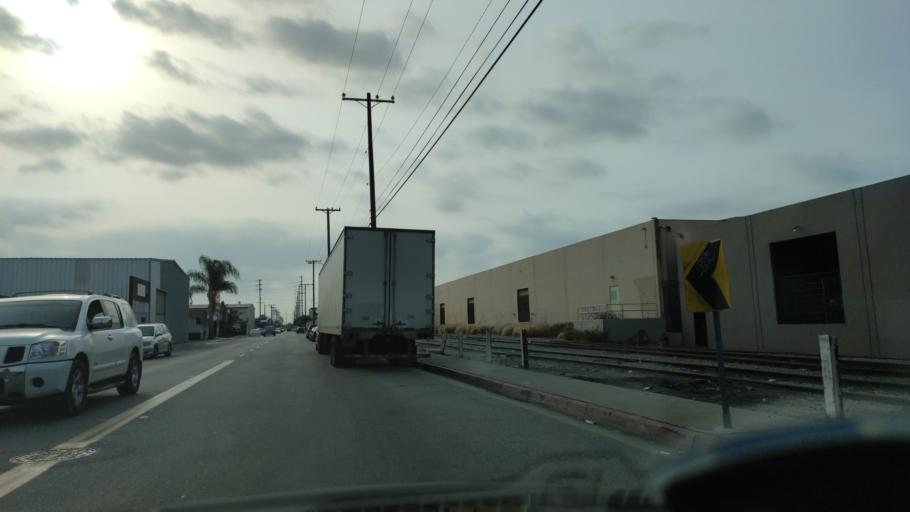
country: US
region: California
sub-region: Los Angeles County
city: Maywood
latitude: 33.9958
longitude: -118.1946
